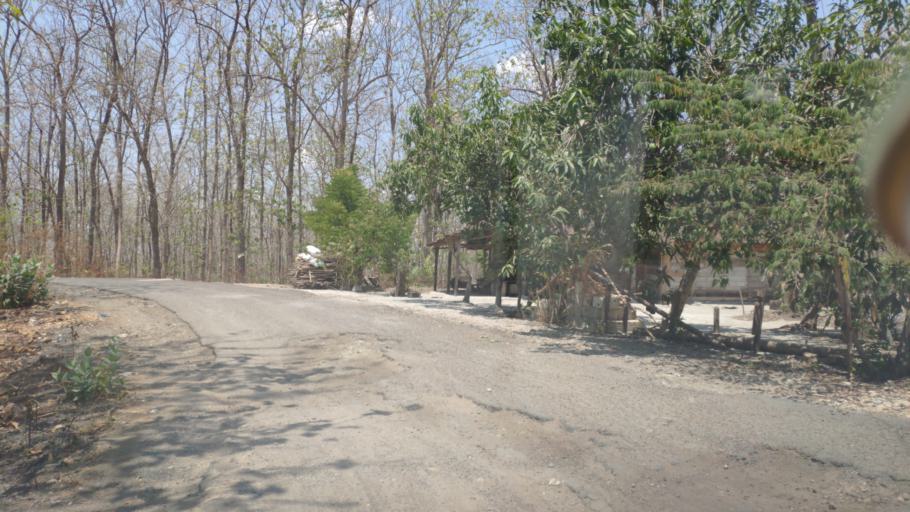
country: ID
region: Central Java
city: Randublatung
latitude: -7.2574
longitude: 111.3776
